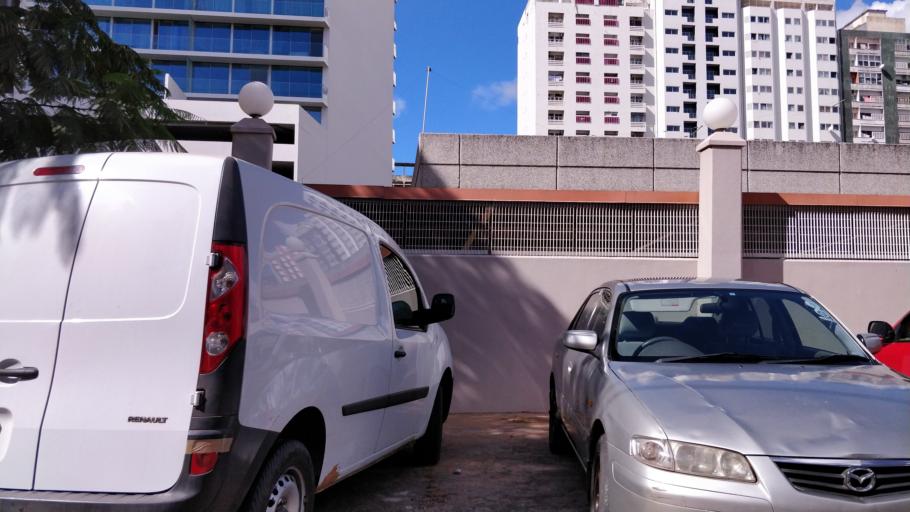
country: MZ
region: Maputo City
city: Maputo
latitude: -25.9728
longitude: 32.5937
